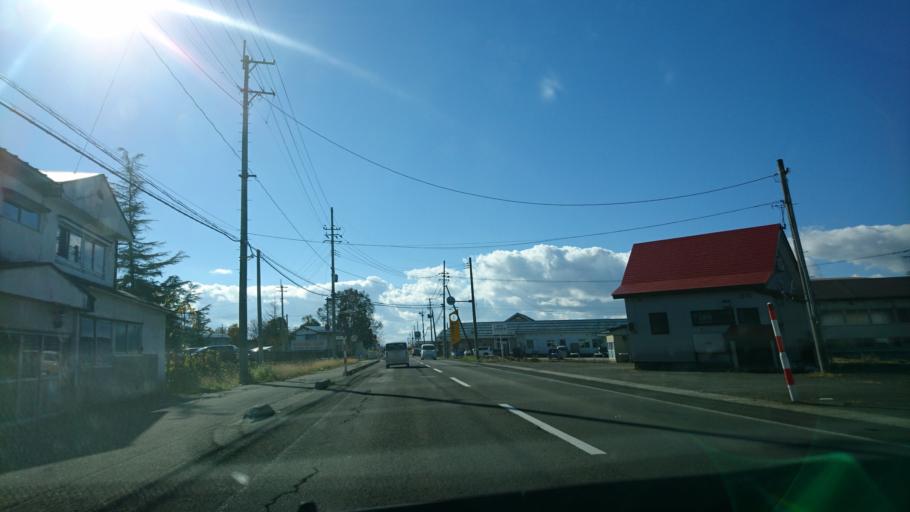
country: JP
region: Akita
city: Yokotemachi
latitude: 39.2731
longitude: 140.5005
